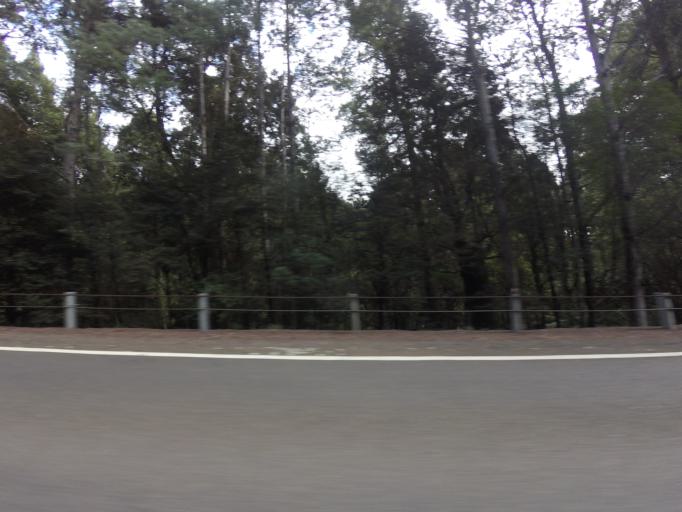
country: AU
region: Tasmania
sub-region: Meander Valley
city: Deloraine
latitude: -41.6556
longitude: 146.7238
